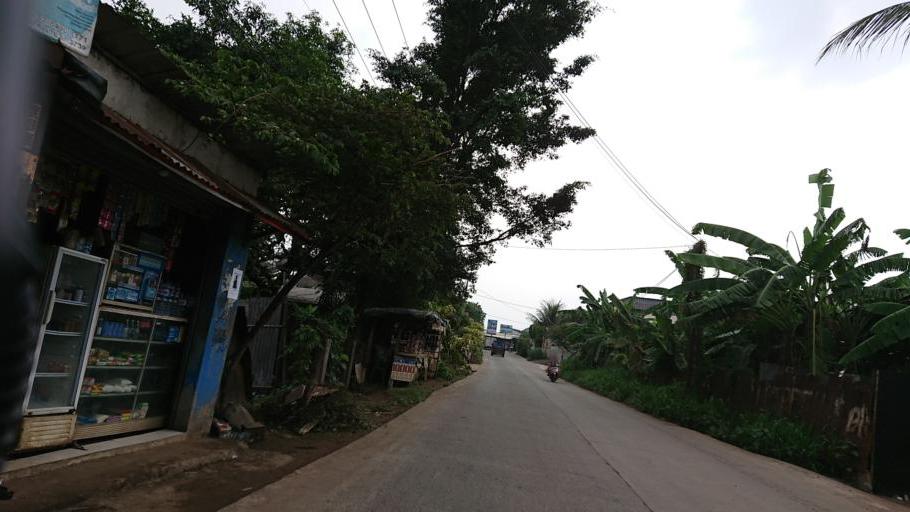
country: ID
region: West Java
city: Parung
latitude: -6.3899
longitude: 106.6834
